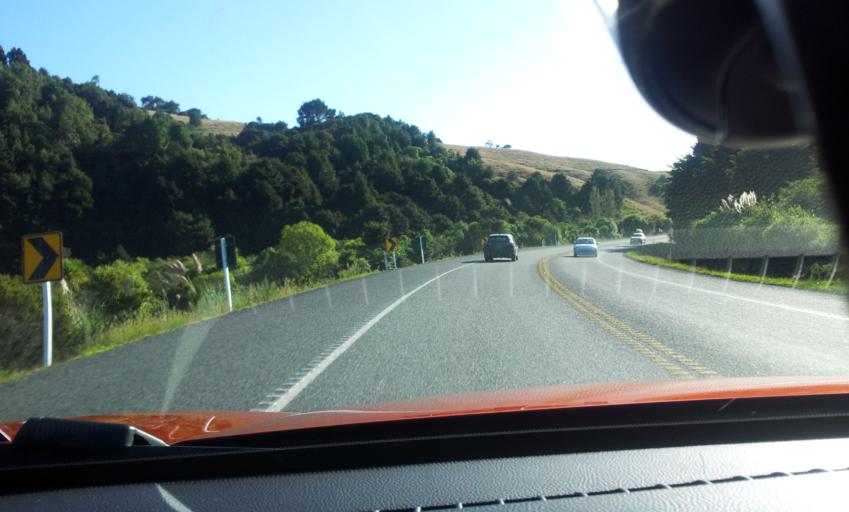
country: NZ
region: Waikato
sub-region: Hauraki District
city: Ngatea
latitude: -37.2805
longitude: 175.3246
